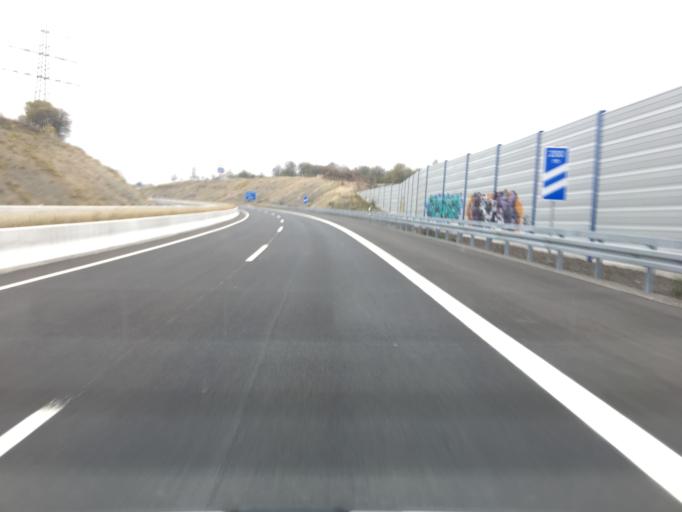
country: DE
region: North Rhine-Westphalia
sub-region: Regierungsbezirk Dusseldorf
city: Velbert
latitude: 51.3253
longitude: 7.0107
